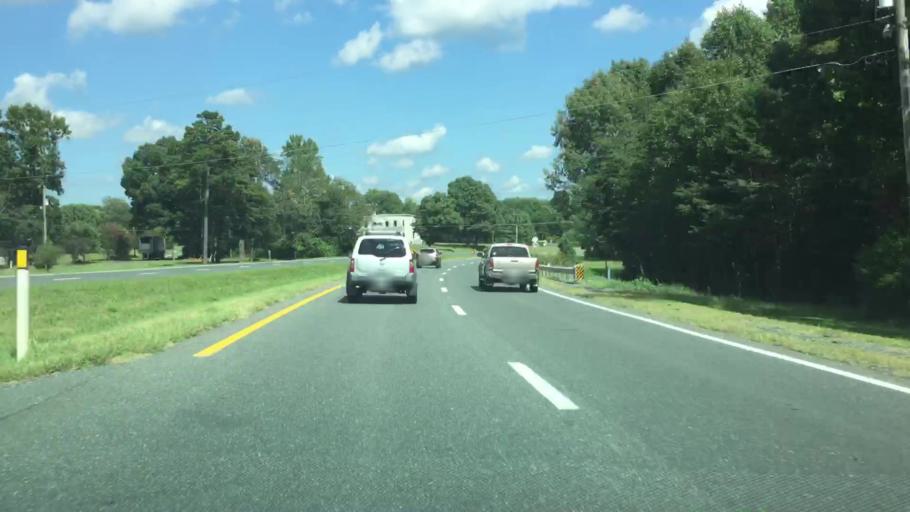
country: US
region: Virginia
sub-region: Campbell County
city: Concord
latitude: 37.3505
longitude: -78.9486
